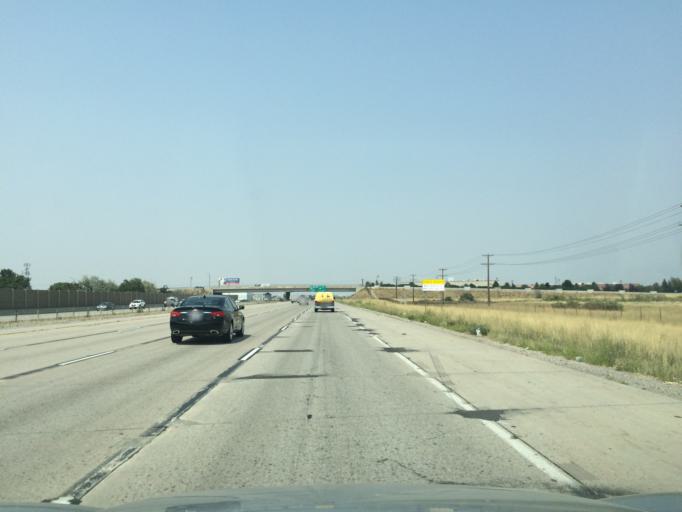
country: US
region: Utah
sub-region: Salt Lake County
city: Taylorsville
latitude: 40.7091
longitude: -111.9532
